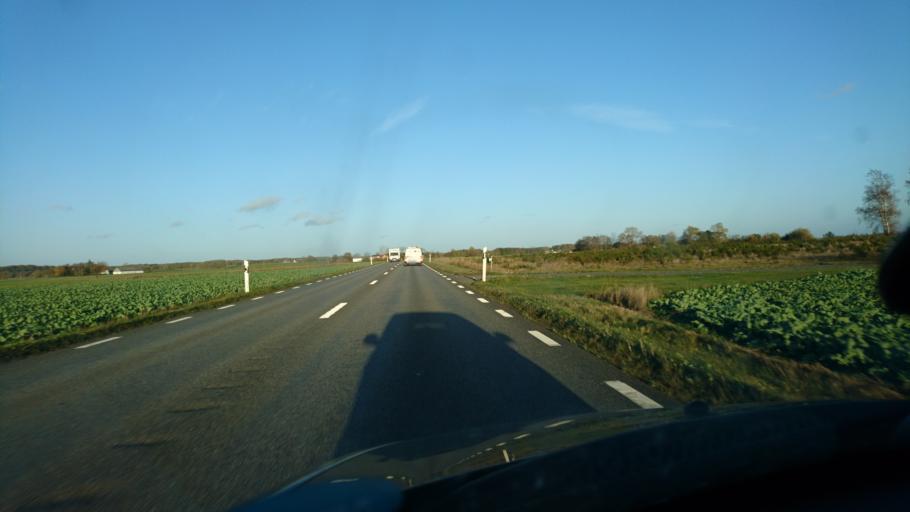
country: SE
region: Skane
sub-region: Tomelilla Kommun
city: Tomelilla
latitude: 55.5478
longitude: 14.0594
